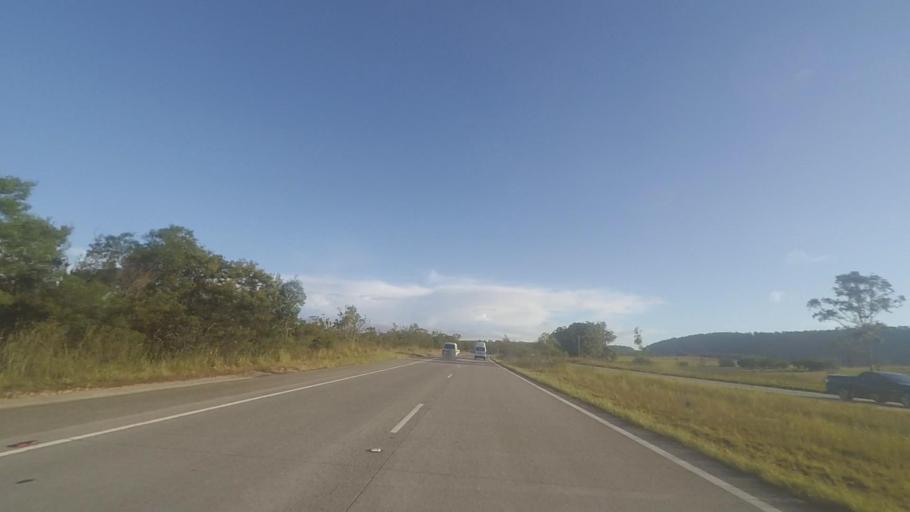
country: AU
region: New South Wales
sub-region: Great Lakes
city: Bulahdelah
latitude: -32.4500
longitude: 152.1969
